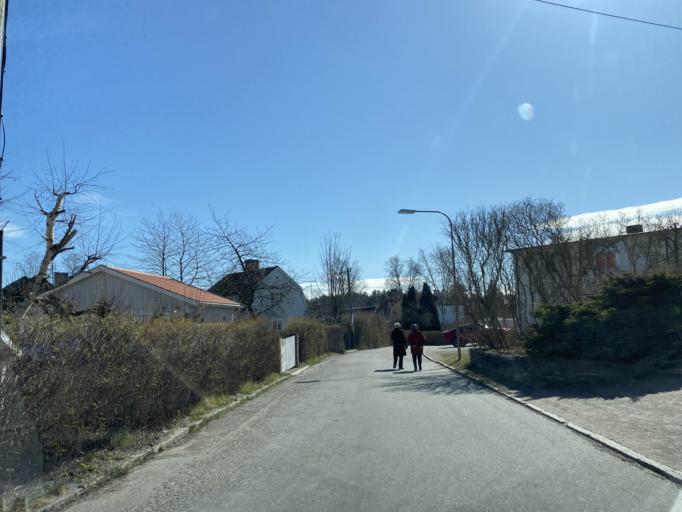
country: SE
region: Stockholm
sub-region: Stockholms Kommun
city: Arsta
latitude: 59.2808
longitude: 18.0562
